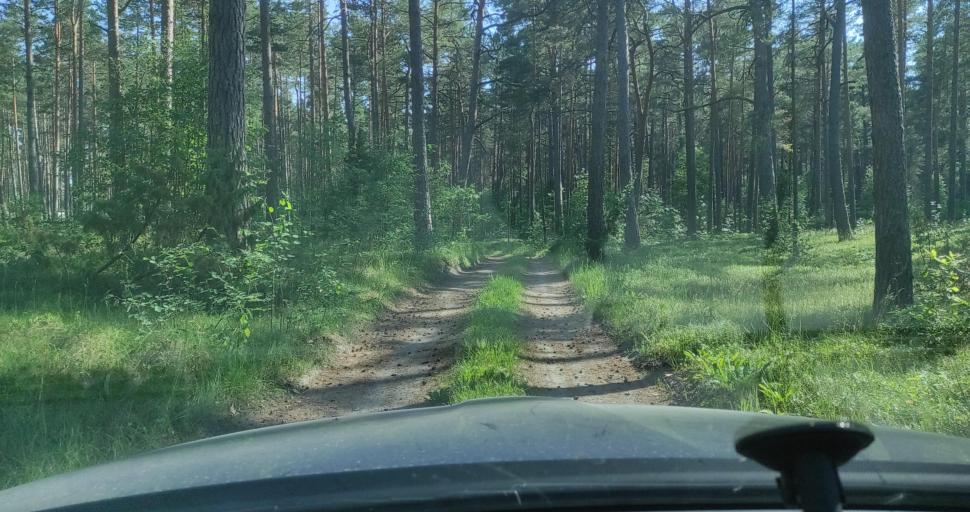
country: LV
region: Jurmala
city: Jurmala
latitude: 56.9566
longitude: 23.8005
